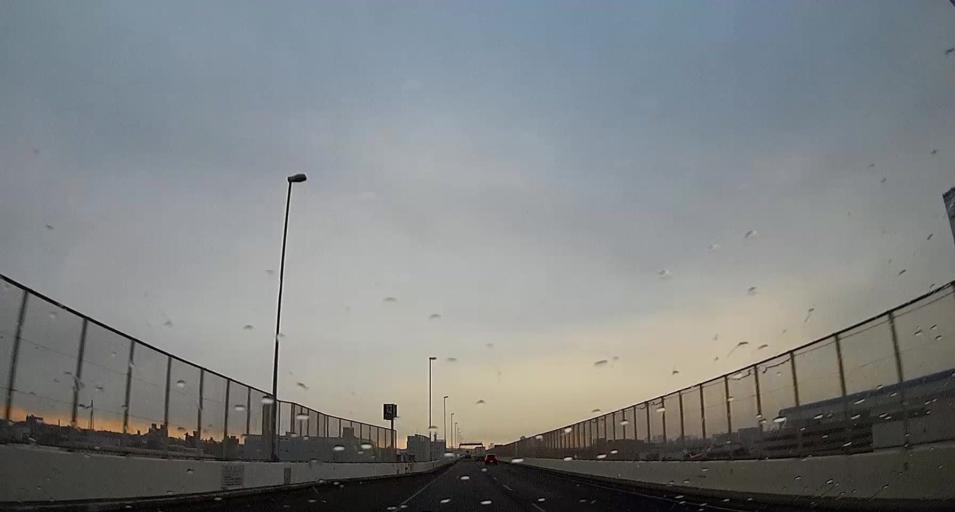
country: JP
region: Kanagawa
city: Yokohama
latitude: 35.4745
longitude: 139.6753
